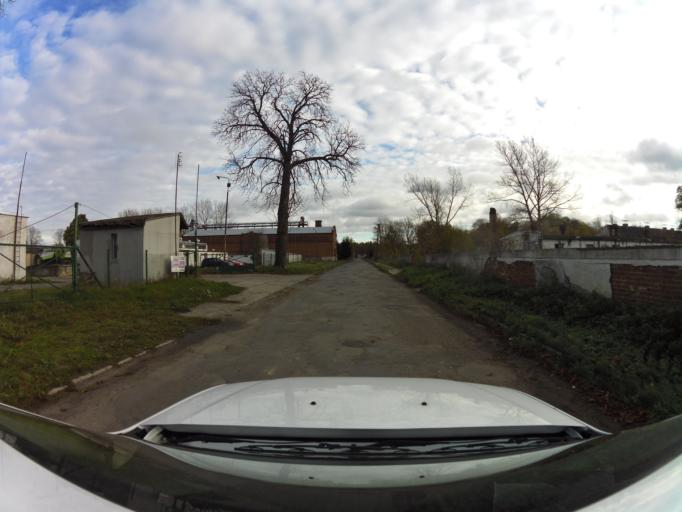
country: PL
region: West Pomeranian Voivodeship
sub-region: Powiat gryficki
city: Gryfice
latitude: 53.9544
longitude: 15.1896
